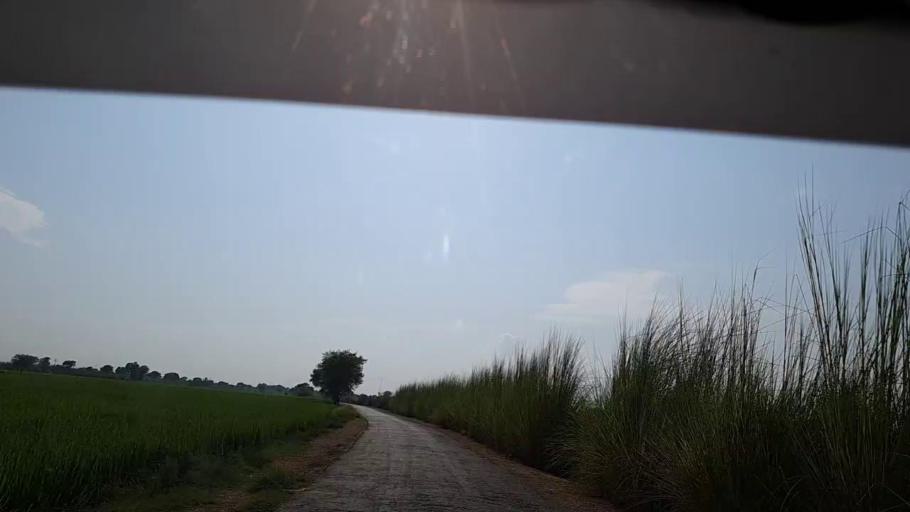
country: PK
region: Sindh
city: Shikarpur
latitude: 28.0896
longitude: 68.6729
